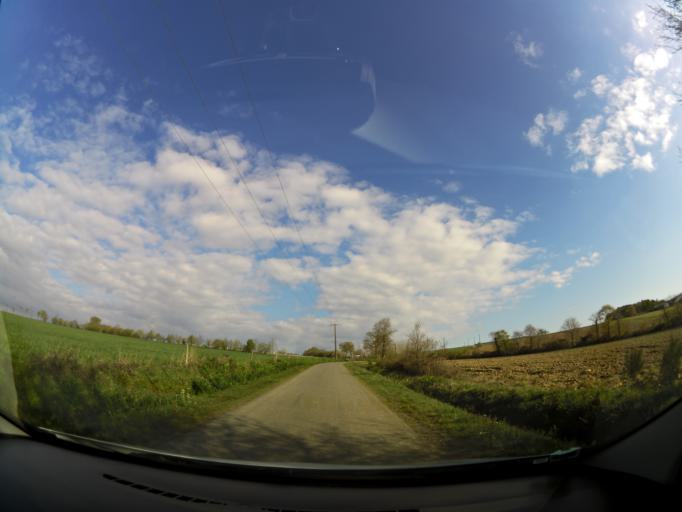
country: FR
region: Brittany
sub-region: Departement d'Ille-et-Vilaine
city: Crevin
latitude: 47.9438
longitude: -1.6989
